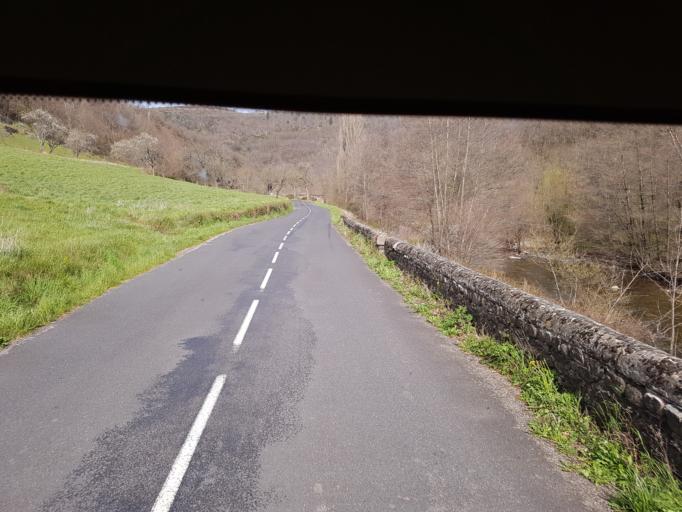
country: FR
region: Languedoc-Roussillon
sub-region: Departement de la Lozere
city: Florac
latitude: 44.2698
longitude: 3.5853
